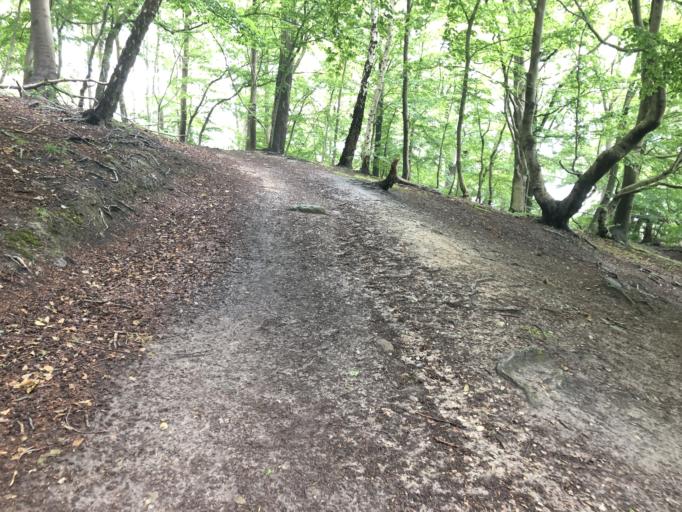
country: DK
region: Capital Region
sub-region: Rudersdal Kommune
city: Holte
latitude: 55.7763
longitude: 12.4461
